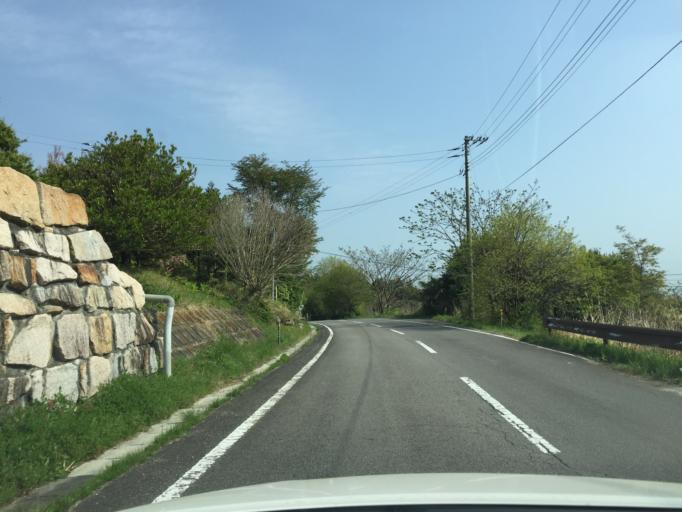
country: JP
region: Fukushima
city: Iwaki
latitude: 37.1577
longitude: 140.8546
